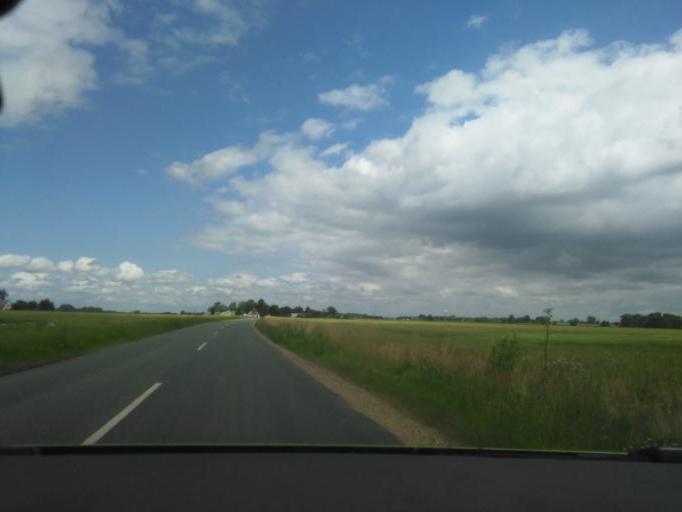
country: DK
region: Zealand
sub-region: Kalundborg Kommune
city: Gorlev
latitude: 55.5451
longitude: 11.1733
